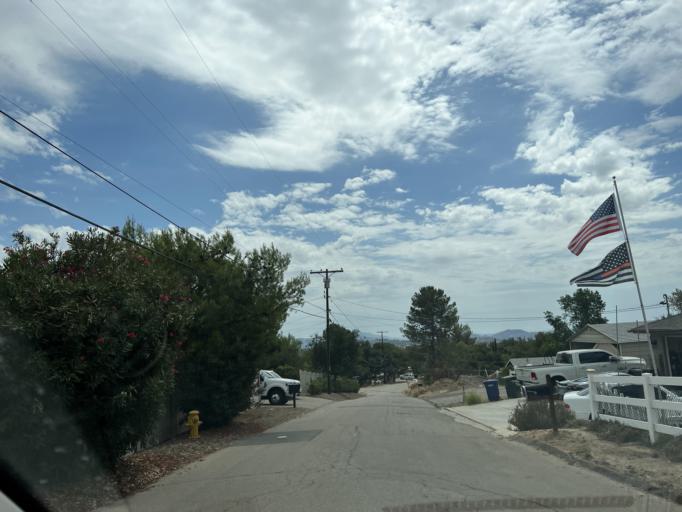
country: US
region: California
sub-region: San Diego County
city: Alpine
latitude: 32.8507
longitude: -116.7461
